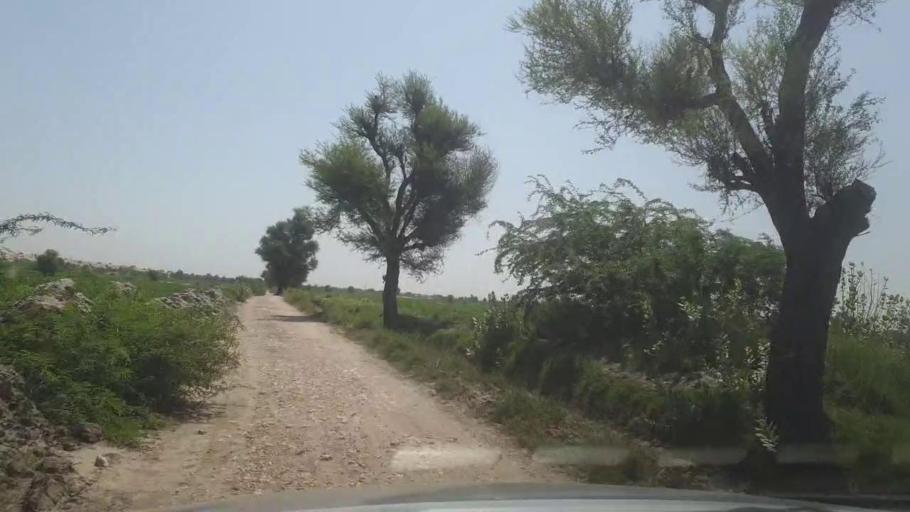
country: PK
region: Sindh
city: Khairpur
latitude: 27.3515
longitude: 69.0508
